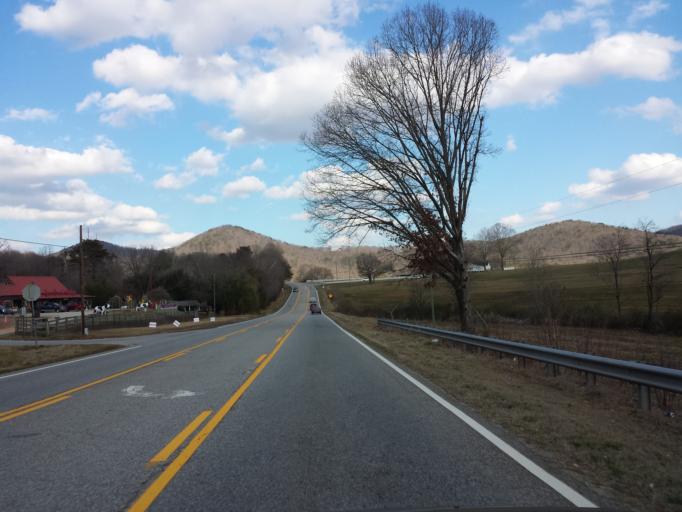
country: US
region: Georgia
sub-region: White County
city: Cleveland
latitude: 34.5497
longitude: -83.7971
